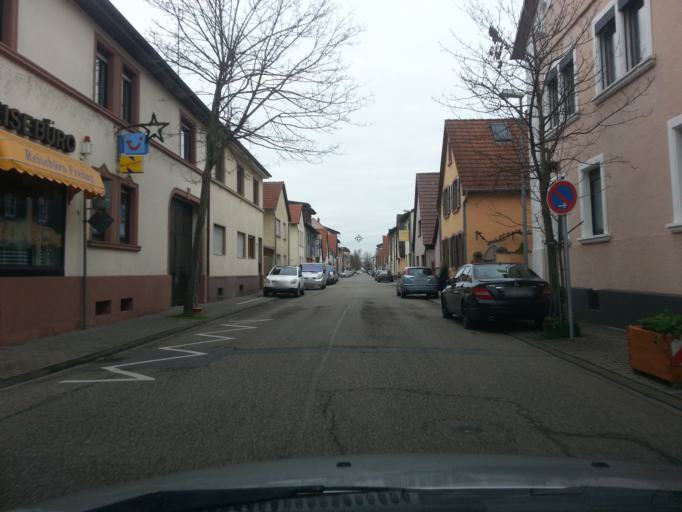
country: DE
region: Baden-Wuerttemberg
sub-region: Karlsruhe Region
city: Reilingen
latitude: 49.2952
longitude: 8.5735
